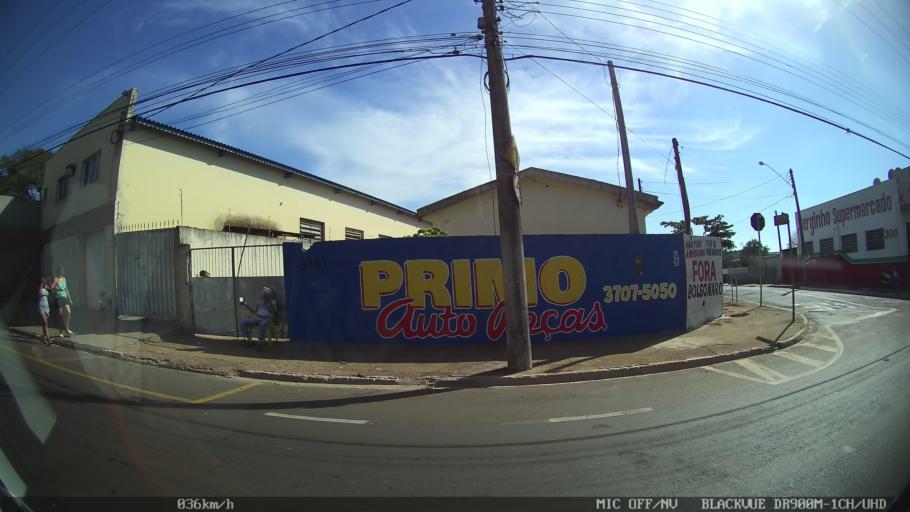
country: BR
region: Sao Paulo
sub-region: Franca
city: Franca
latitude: -20.4979
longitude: -47.3985
